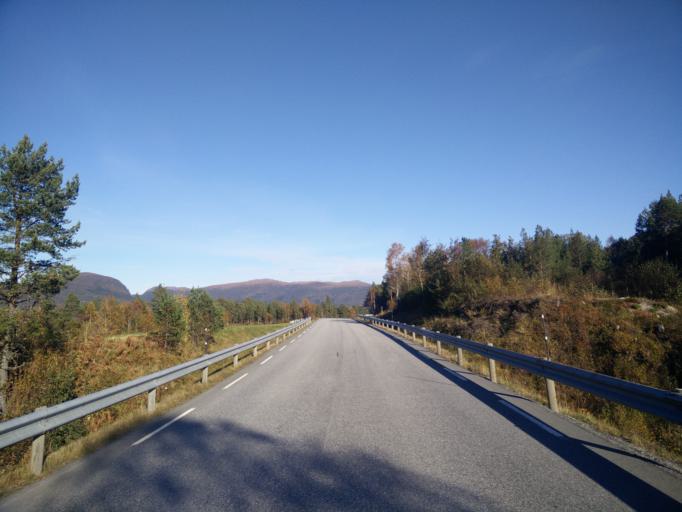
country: NO
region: More og Romsdal
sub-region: Halsa
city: Liaboen
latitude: 63.1275
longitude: 8.3751
